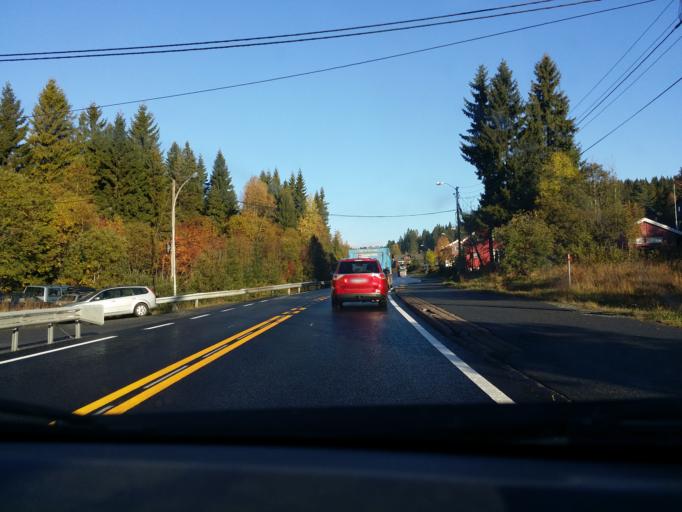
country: NO
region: Akershus
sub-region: Baerum
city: Skui
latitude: 59.9594
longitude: 10.3608
